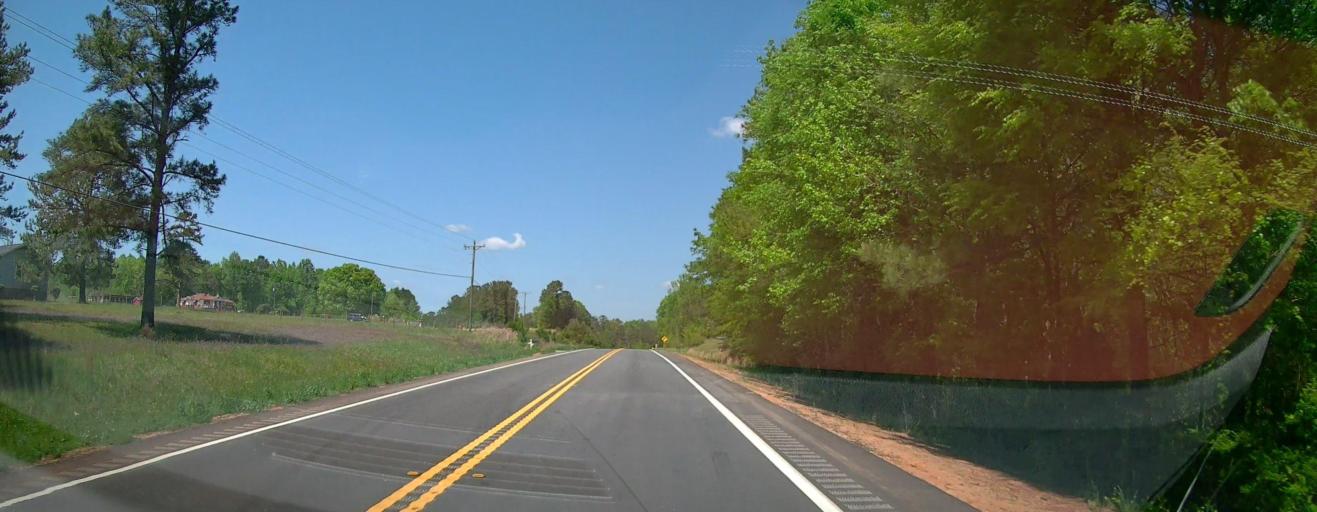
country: US
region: Georgia
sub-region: Putnam County
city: Eatonton
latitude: 33.2514
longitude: -83.4282
